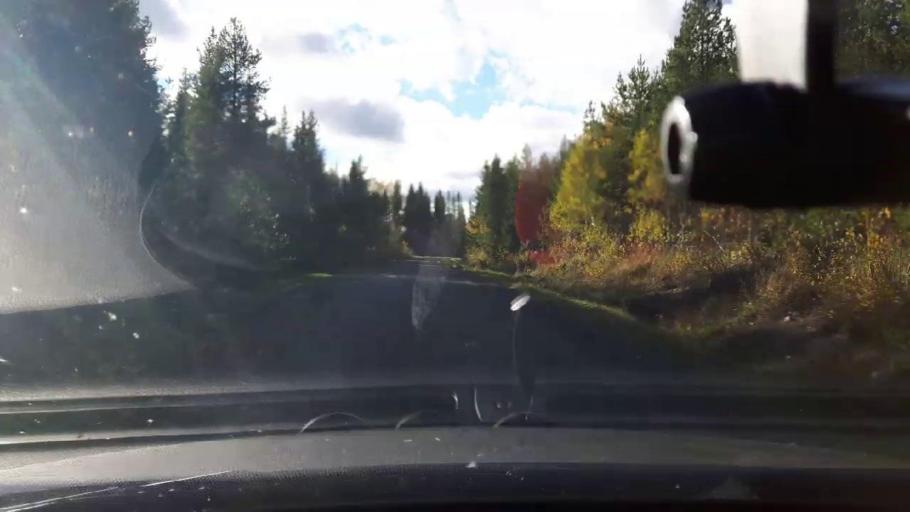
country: SE
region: Jaemtland
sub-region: Bergs Kommun
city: Hoverberg
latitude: 63.0207
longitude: 14.3222
